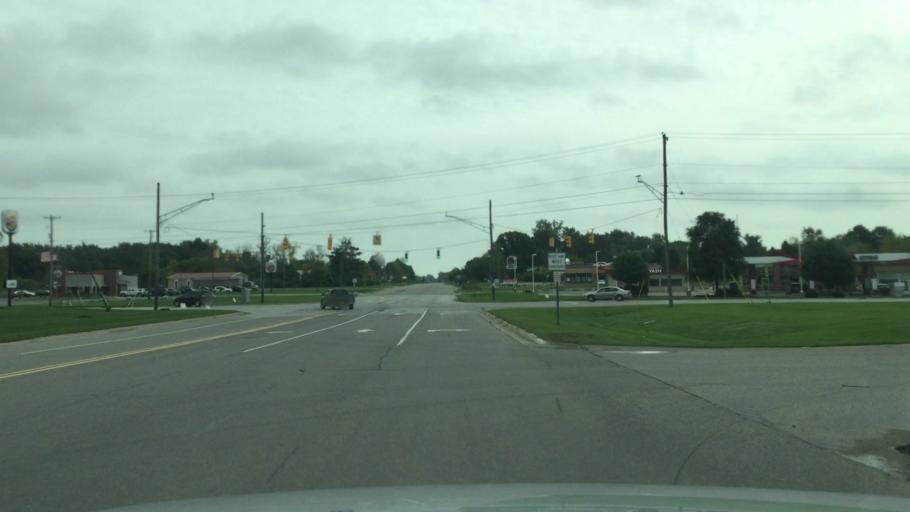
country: US
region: Michigan
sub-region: Shiawassee County
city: Perry
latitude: 42.8356
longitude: -84.2208
